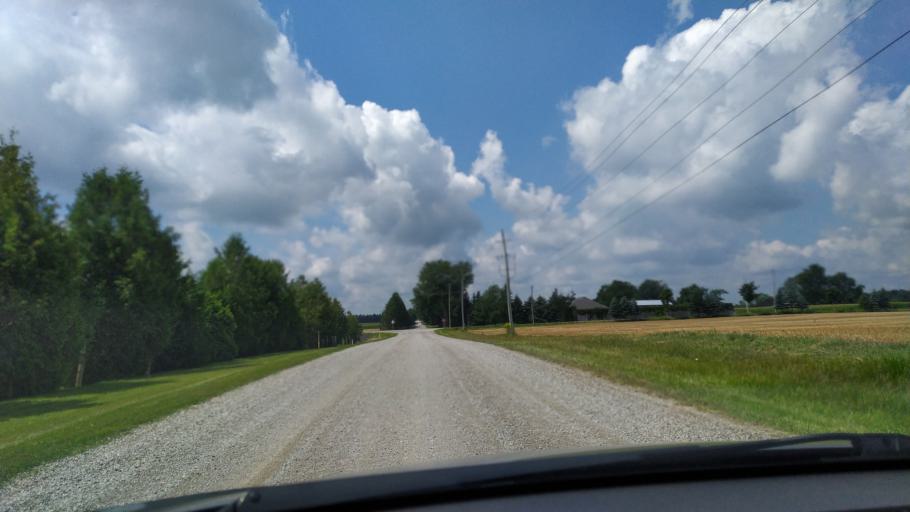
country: CA
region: Ontario
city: London
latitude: 43.0777
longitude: -81.3391
